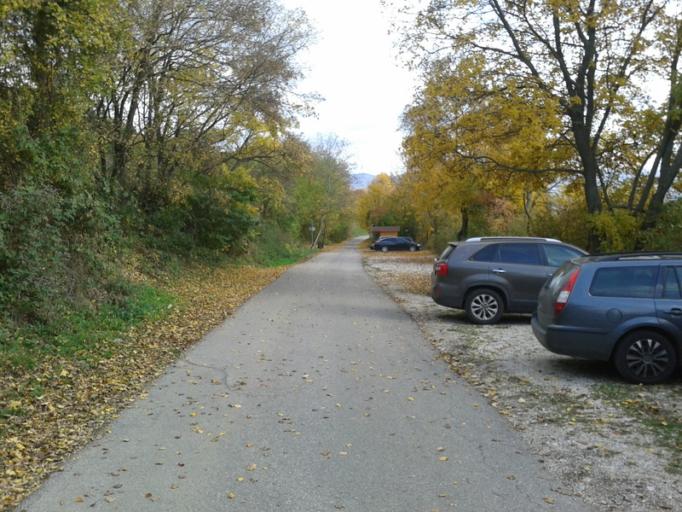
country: SK
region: Nitriansky
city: Cachtice
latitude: 48.7170
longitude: 17.7700
